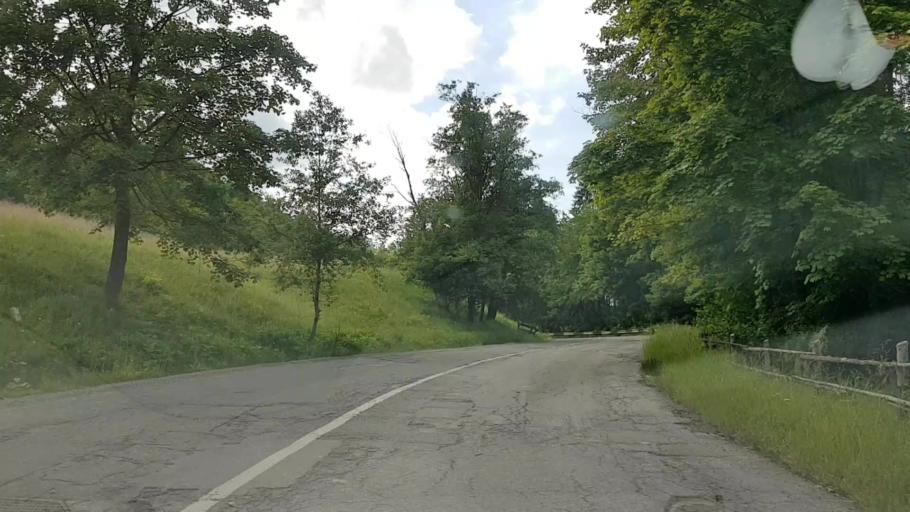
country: RO
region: Neamt
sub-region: Comuna Pangarati
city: Pangarati
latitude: 46.9347
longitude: 26.1252
